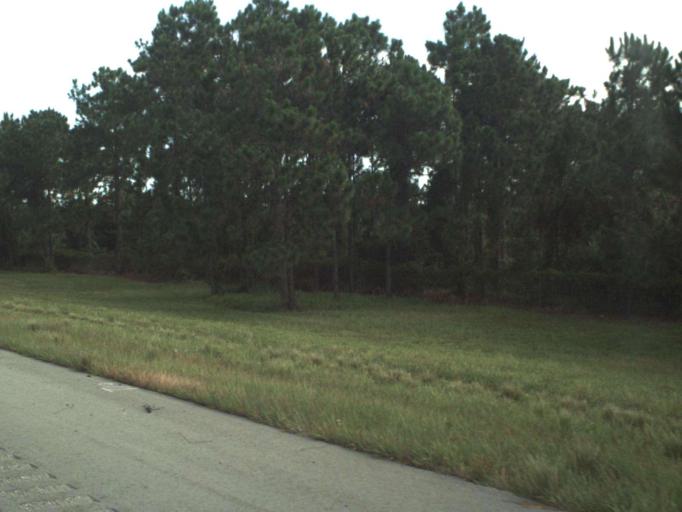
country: US
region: Florida
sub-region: Saint Lucie County
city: Lakewood Park
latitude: 27.4796
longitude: -80.4328
